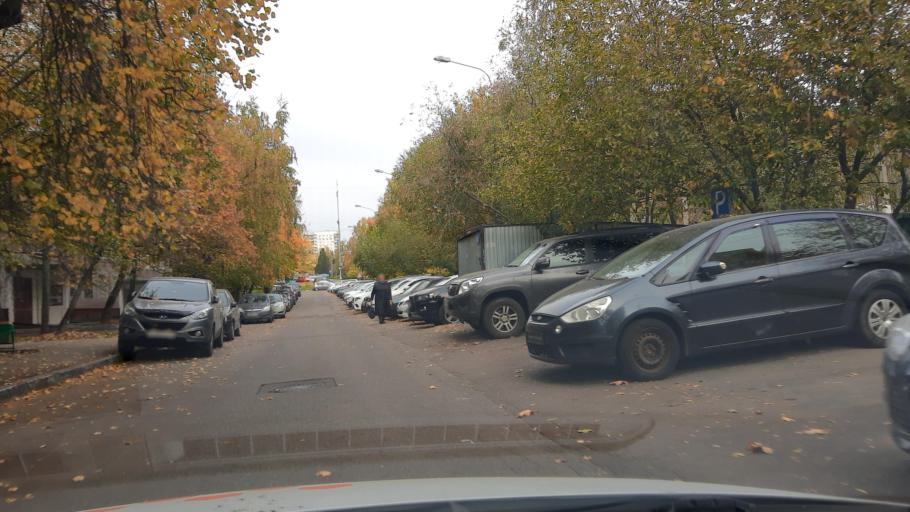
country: RU
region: Moscow
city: Yasenevo
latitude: 55.6050
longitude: 37.5539
